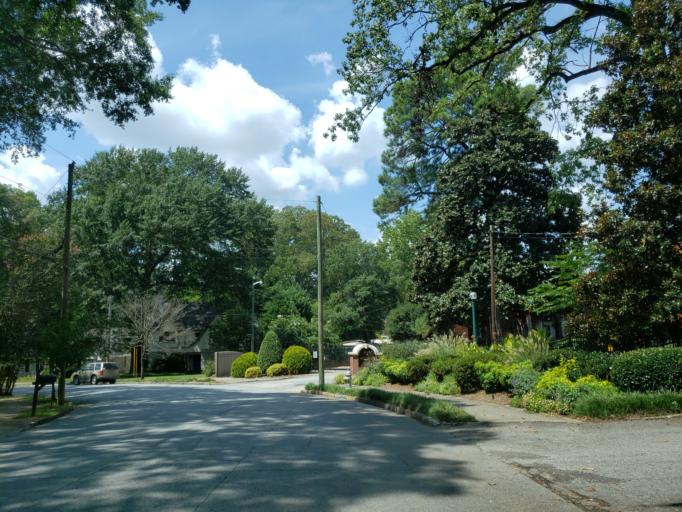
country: US
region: Georgia
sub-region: DeKalb County
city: Druid Hills
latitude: 33.7894
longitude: -84.3645
